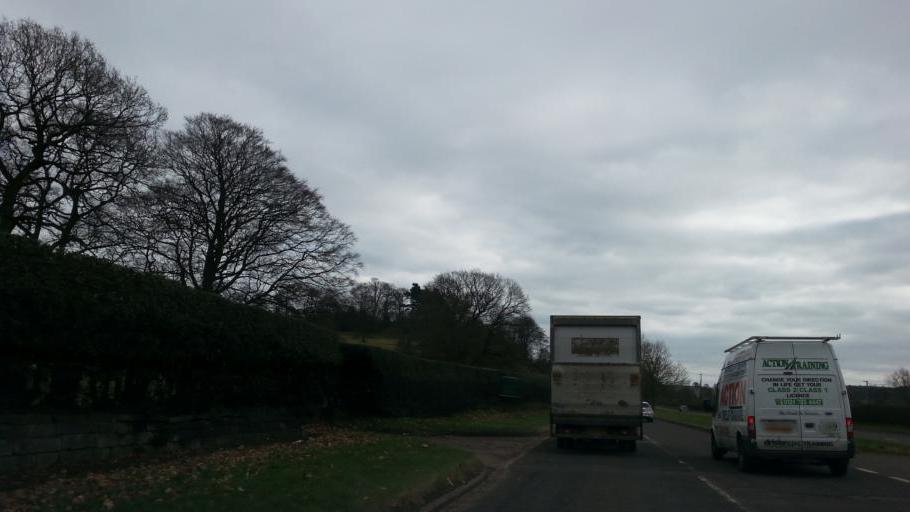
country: GB
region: England
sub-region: Staffordshire
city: Stafford
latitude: 52.8578
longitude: -2.0749
